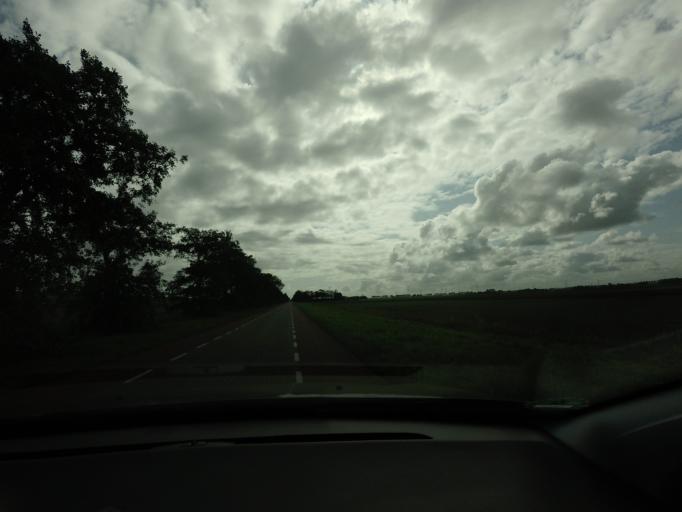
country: NL
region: North Holland
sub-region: Gemeente Hollands Kroon
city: Den Oever
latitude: 52.8722
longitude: 5.0904
